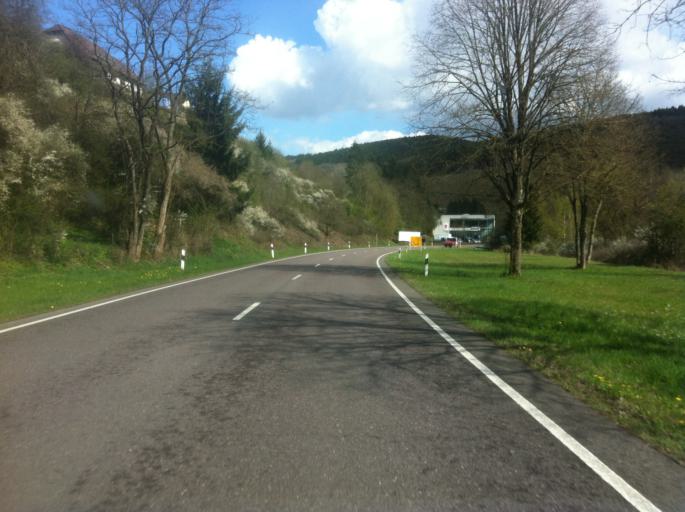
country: LU
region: Diekirch
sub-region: Canton de Wiltz
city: Esch-sur-Sure
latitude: 49.9332
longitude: 5.9363
